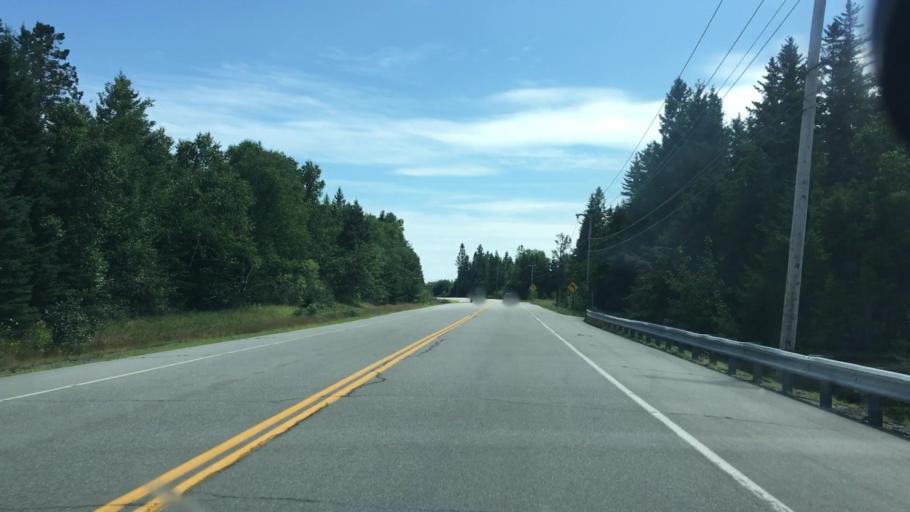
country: US
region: Maine
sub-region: Washington County
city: Eastport
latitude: 44.9451
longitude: -67.0392
